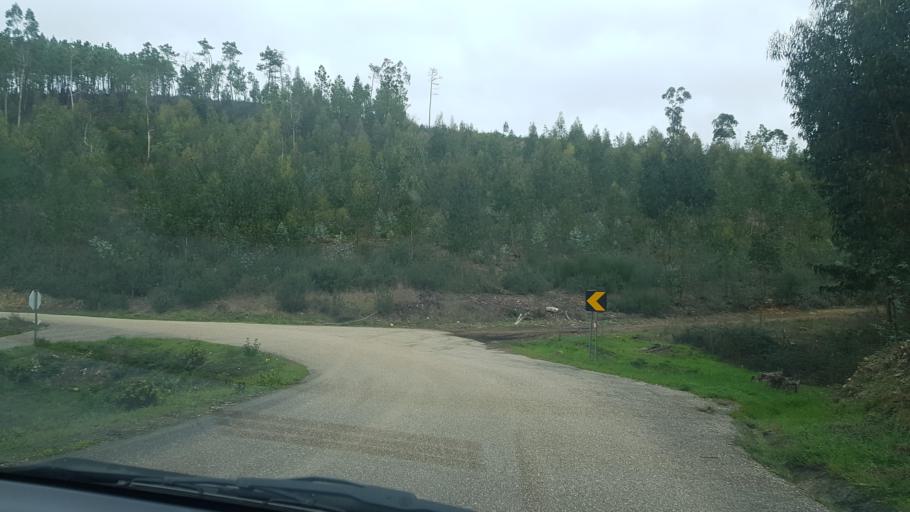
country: PT
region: Castelo Branco
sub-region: Vila de Rei
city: Vila de Rei
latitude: 39.5979
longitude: -8.1174
